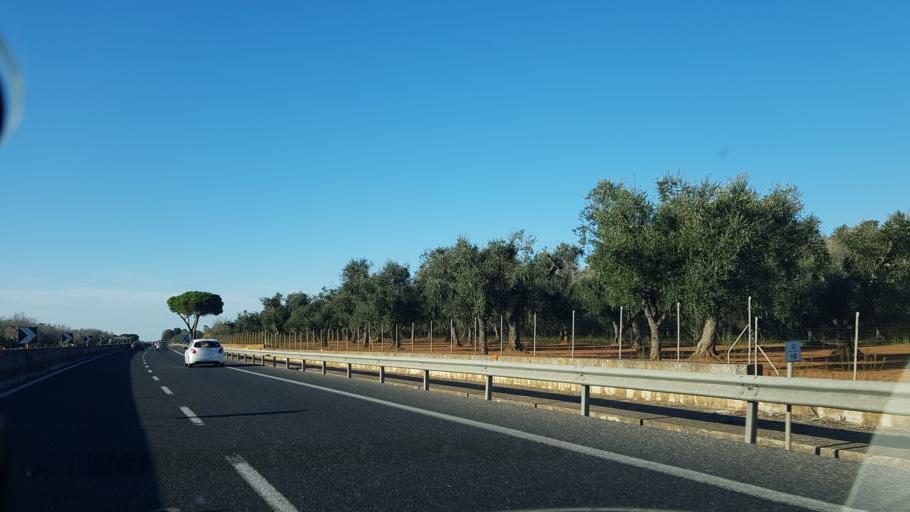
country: IT
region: Apulia
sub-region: Provincia di Brindisi
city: Torchiarolo
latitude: 40.4688
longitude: 18.0524
